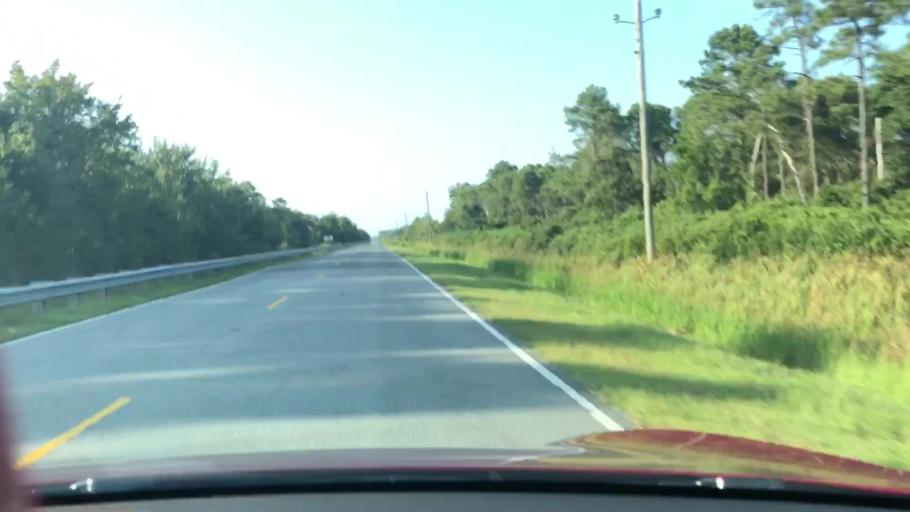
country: US
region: North Carolina
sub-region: Dare County
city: Wanchese
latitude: 35.7471
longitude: -75.7687
